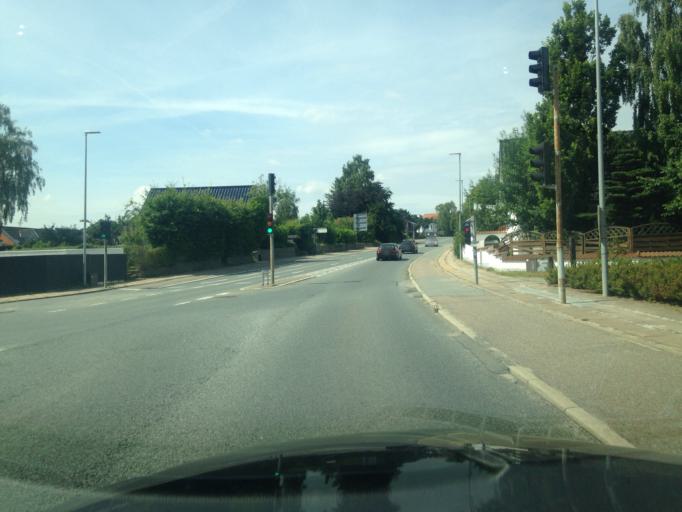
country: DK
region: South Denmark
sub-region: Kolding Kommune
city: Kolding
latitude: 55.4956
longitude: 9.4773
